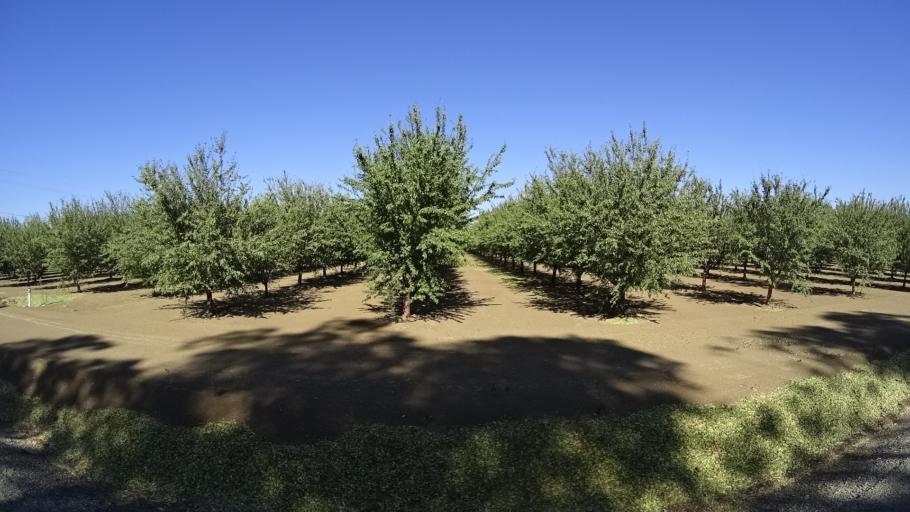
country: US
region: California
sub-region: Yolo County
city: Cottonwood
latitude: 38.6198
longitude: -121.8718
